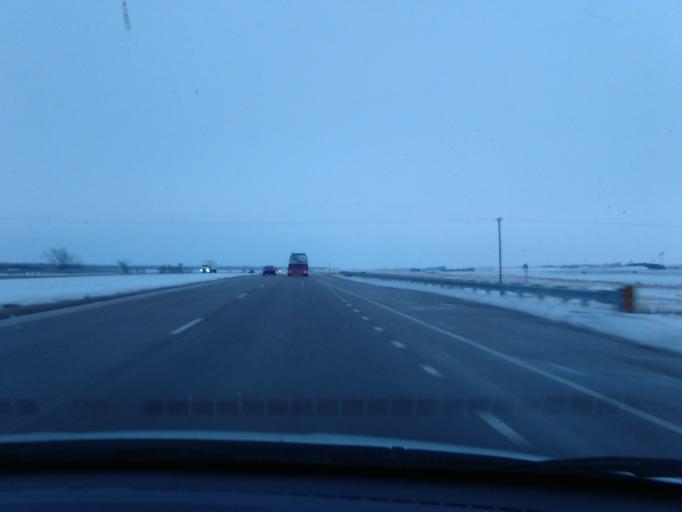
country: US
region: Nebraska
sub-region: Lincoln County
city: Sutherland
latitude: 41.1116
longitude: -101.3502
